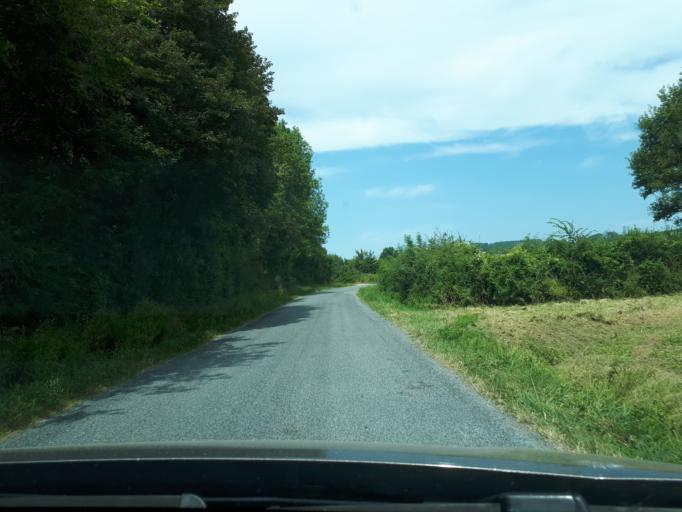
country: FR
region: Centre
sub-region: Departement du Cher
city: Sancerre
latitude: 47.2973
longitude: 2.7488
